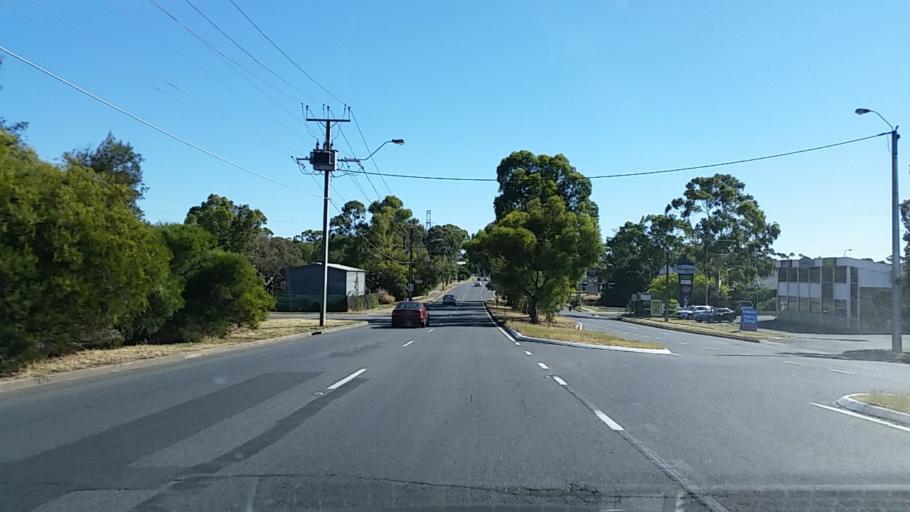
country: AU
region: South Australia
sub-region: Salisbury
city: Ingle Farm
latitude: -34.8352
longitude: 138.6261
